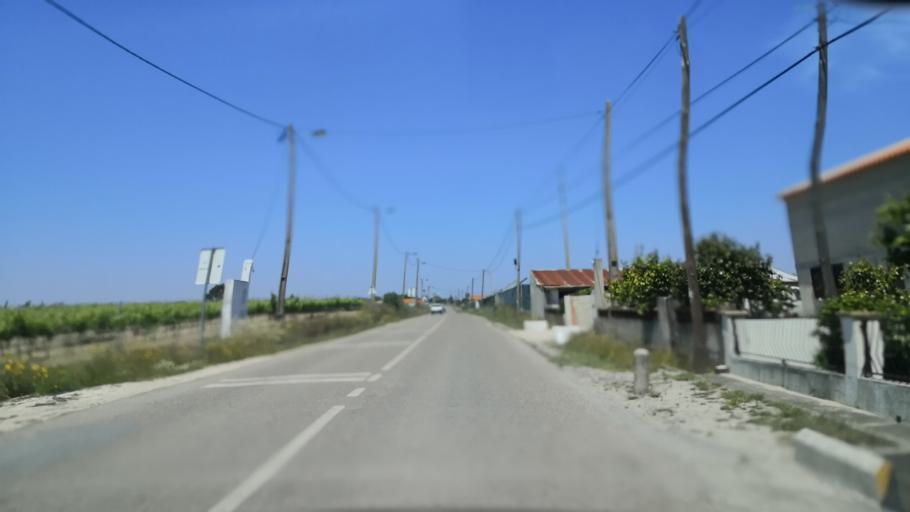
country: PT
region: Santarem
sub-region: Benavente
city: Poceirao
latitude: 38.6667
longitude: -8.7370
